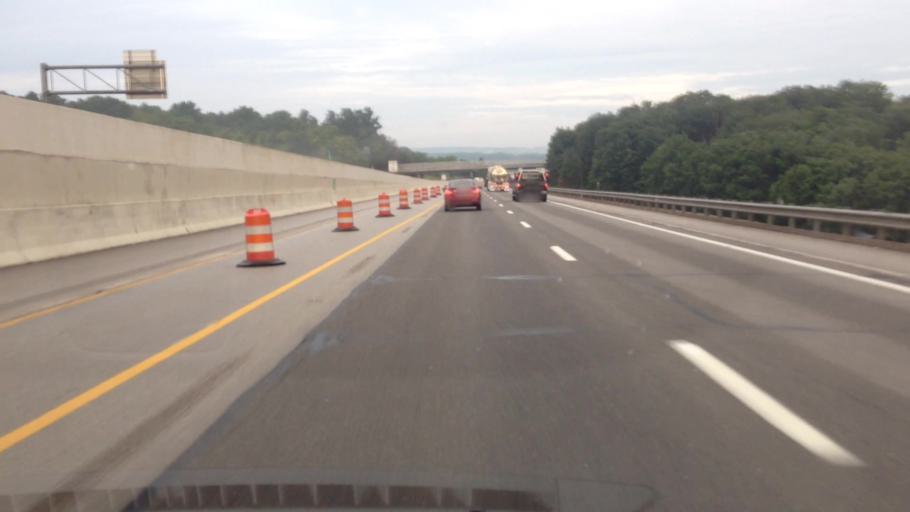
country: US
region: Ohio
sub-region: Summit County
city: Boston Heights
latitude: 41.2570
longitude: -81.5348
